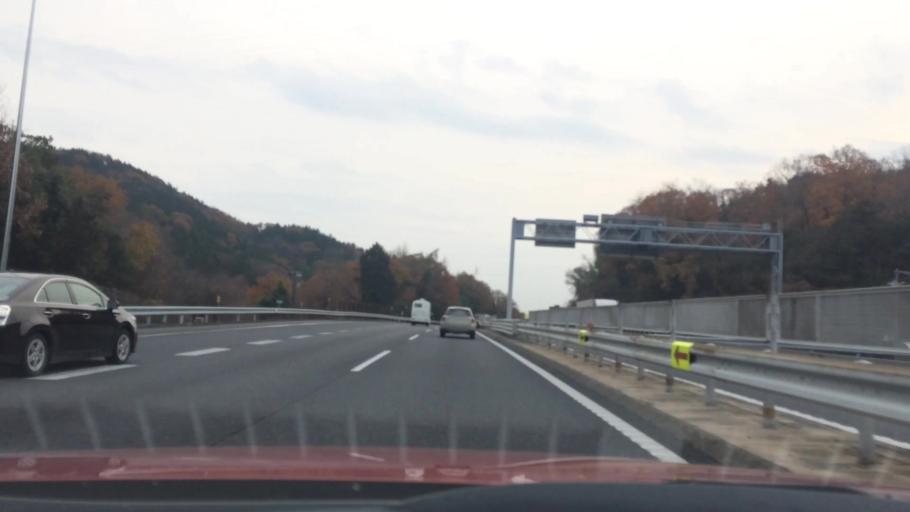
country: JP
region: Aichi
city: Kasugai
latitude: 35.3267
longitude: 137.0242
